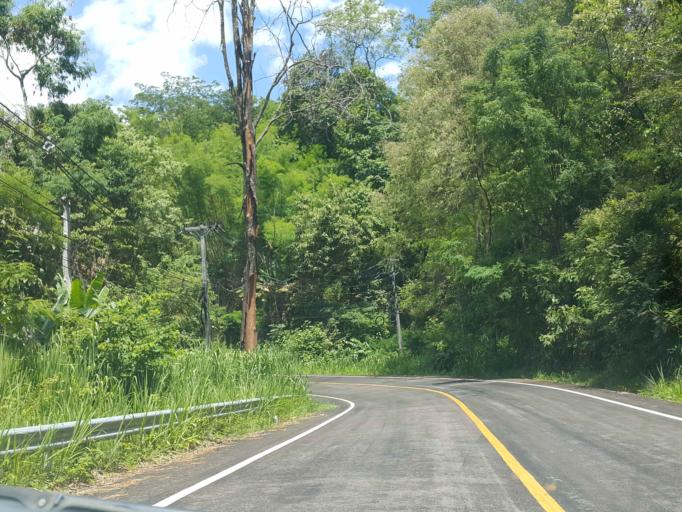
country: TH
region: Chiang Mai
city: Samoeng
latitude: 18.8541
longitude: 98.7730
